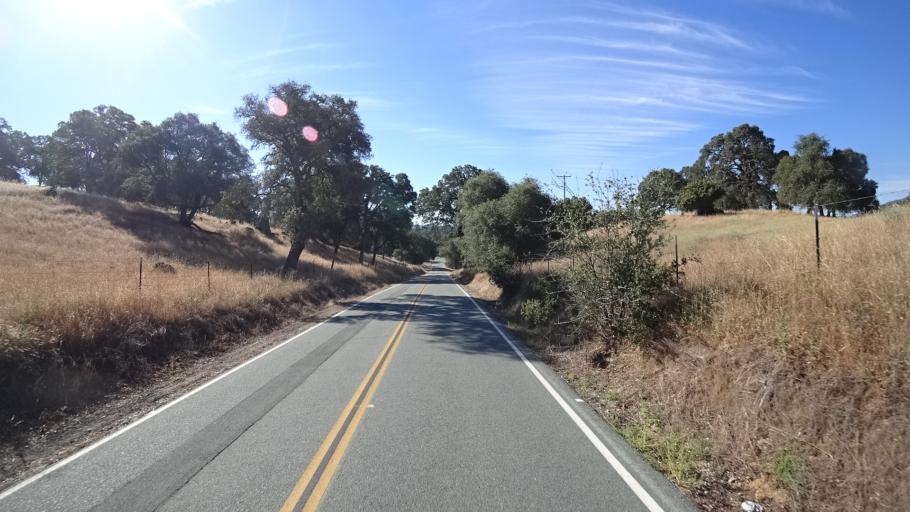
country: US
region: California
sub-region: Calaveras County
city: San Andreas
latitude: 38.1824
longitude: -120.6556
